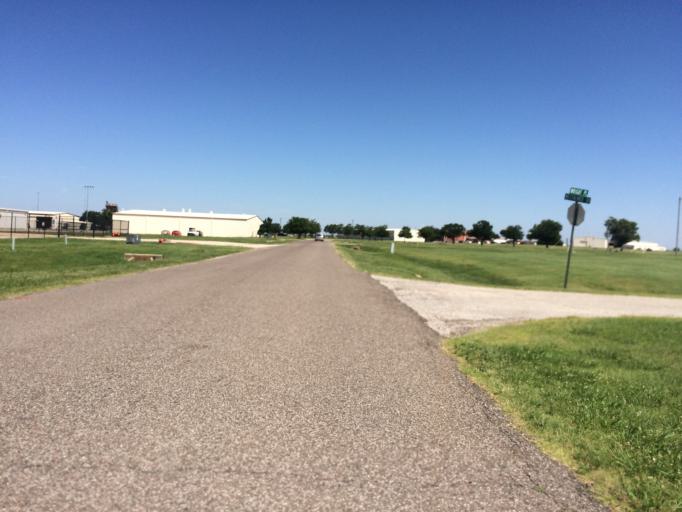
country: US
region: Oklahoma
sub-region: Cleveland County
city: Norman
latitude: 35.2389
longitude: -97.4647
